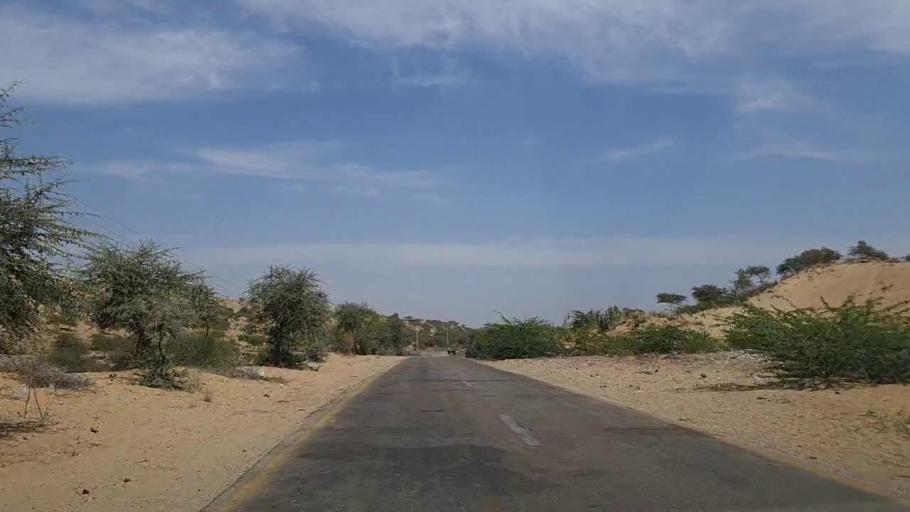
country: PK
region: Sindh
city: Mithi
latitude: 24.7727
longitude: 69.8022
